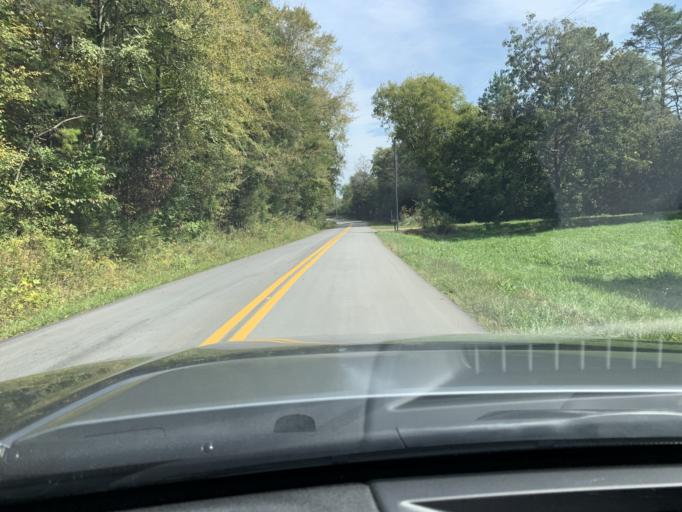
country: US
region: Georgia
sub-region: Polk County
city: Cedartown
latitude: 33.9490
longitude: -85.3565
